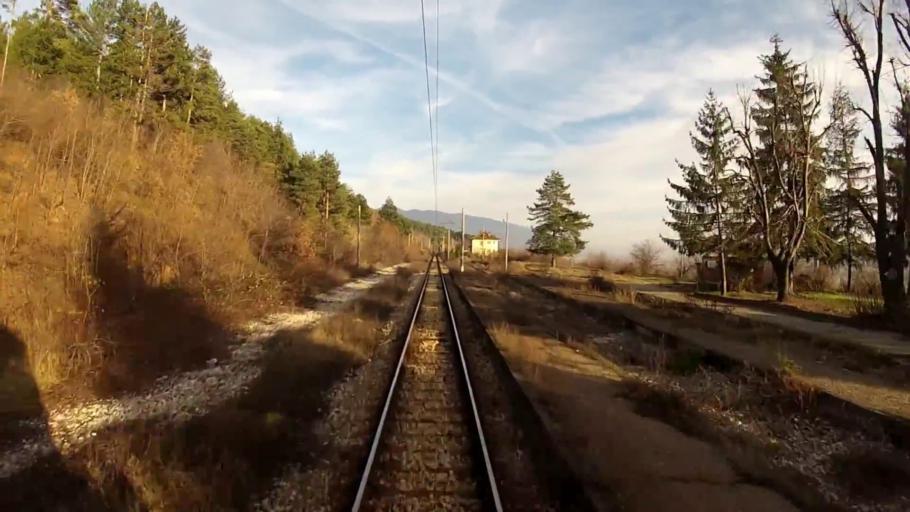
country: BG
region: Plovdiv
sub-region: Obshtina Karlovo
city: Klisura
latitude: 42.7229
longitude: 24.5922
